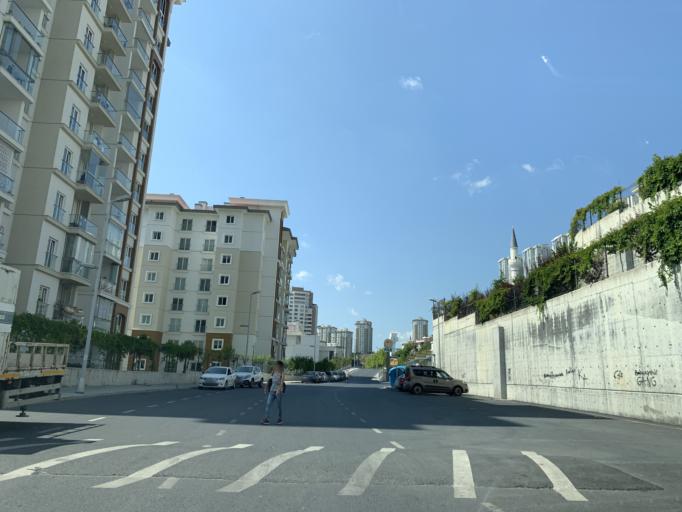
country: TR
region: Istanbul
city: Esenyurt
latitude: 41.0749
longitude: 28.6952
